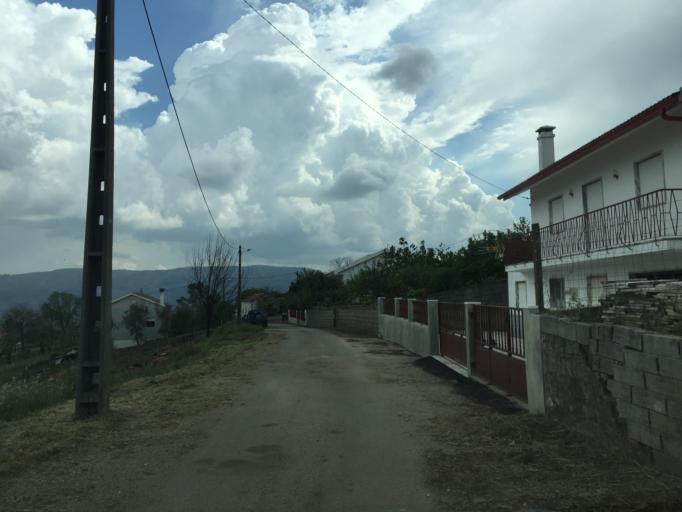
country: PT
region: Coimbra
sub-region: Arganil
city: Arganil
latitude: 40.1613
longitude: -7.9758
